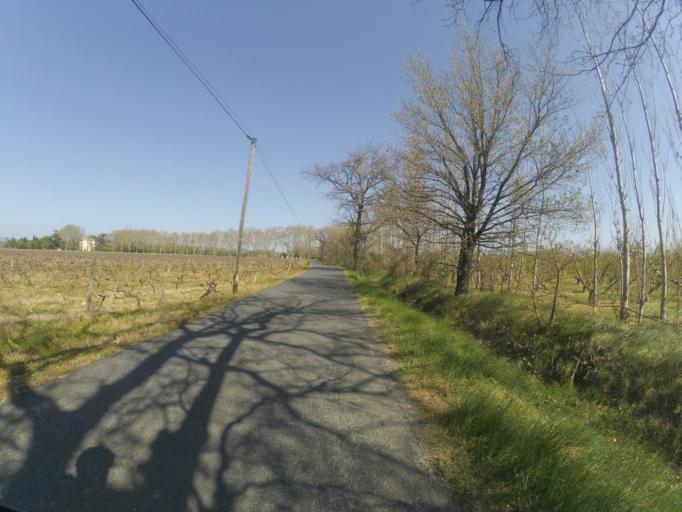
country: FR
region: Languedoc-Roussillon
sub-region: Departement des Pyrenees-Orientales
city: Thuir
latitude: 42.6558
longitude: 2.7597
